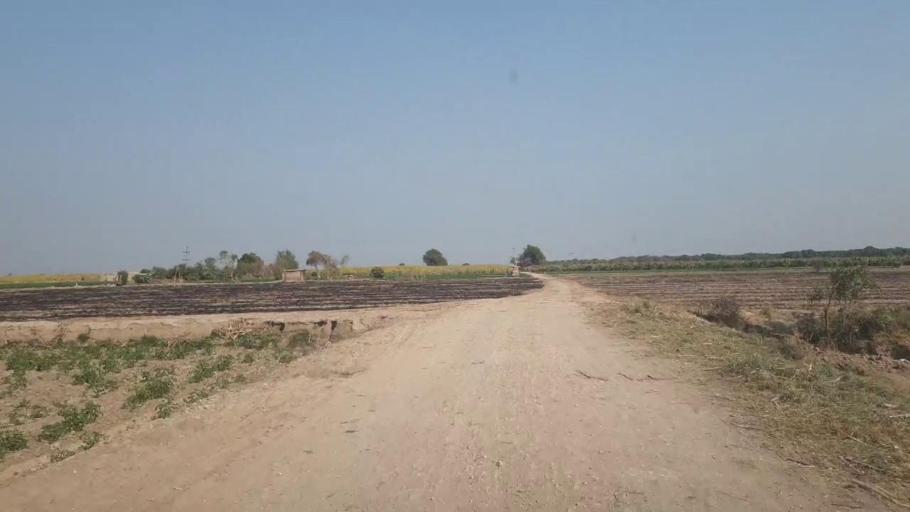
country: PK
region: Sindh
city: Tando Allahyar
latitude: 25.4496
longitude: 68.7947
